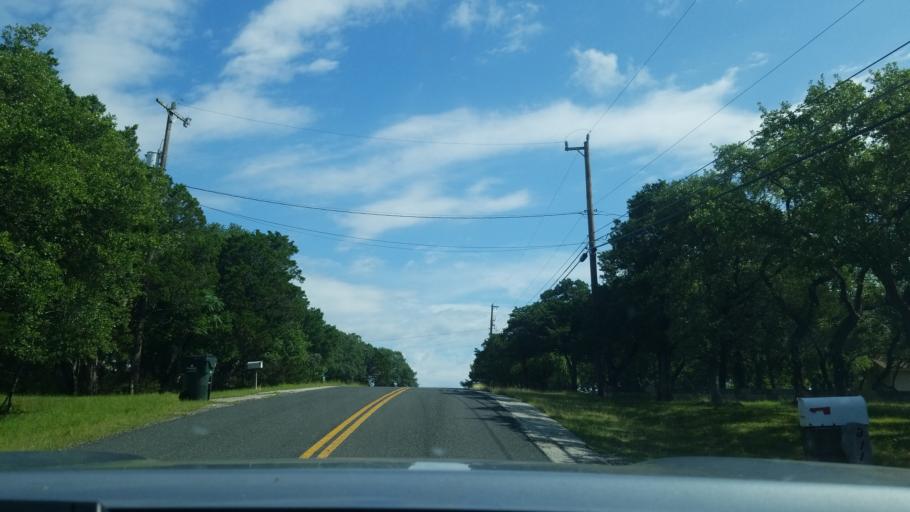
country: US
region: Texas
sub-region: Comal County
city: Bulverde
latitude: 29.7573
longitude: -98.4427
